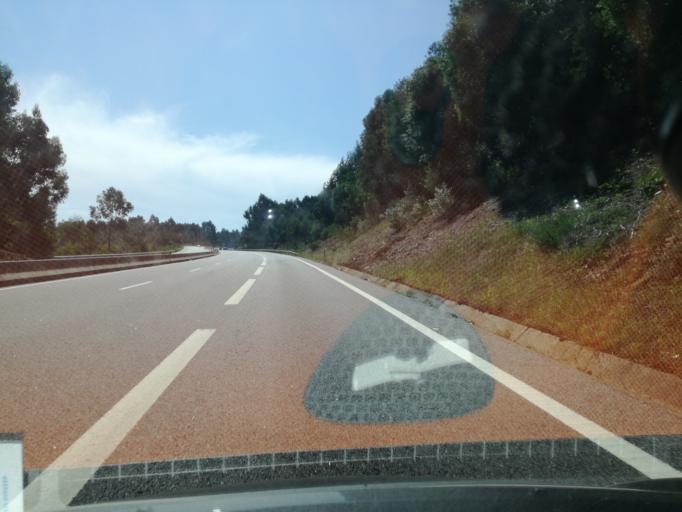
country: PT
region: Viana do Castelo
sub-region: Caminha
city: Vila Praia de Ancora
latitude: 41.7911
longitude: -8.7913
